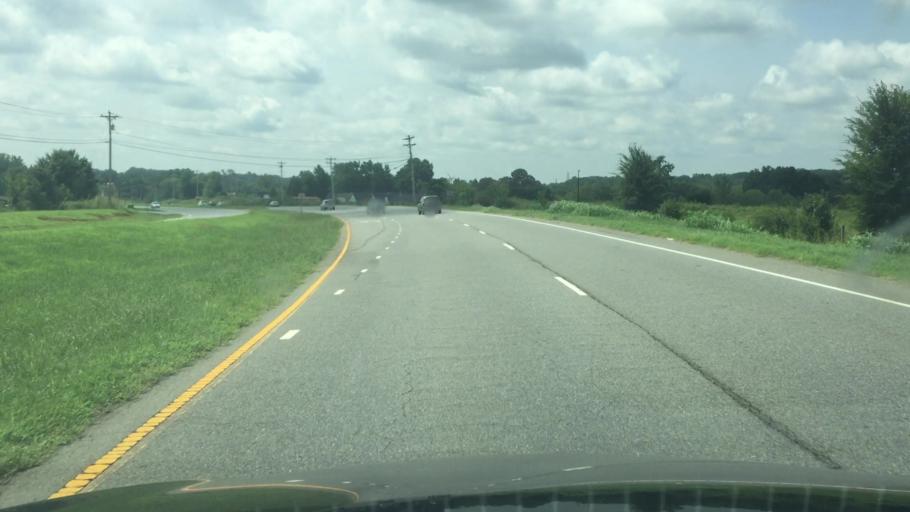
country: US
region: North Carolina
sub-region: Rowan County
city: Enochville
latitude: 35.4832
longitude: -80.6738
